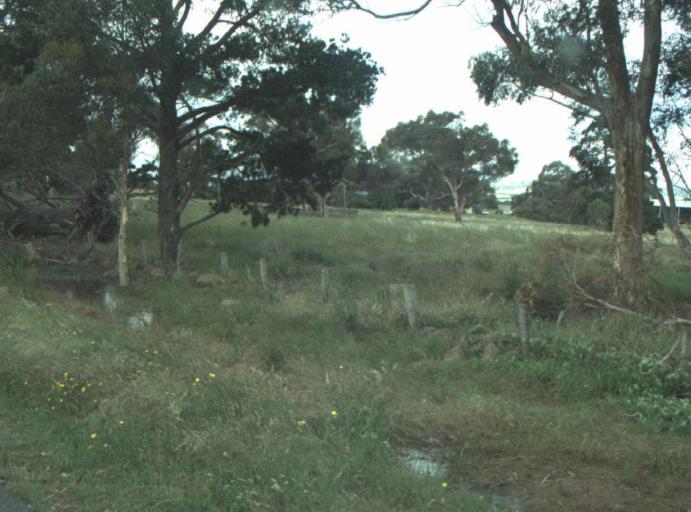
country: AU
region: Victoria
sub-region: Wyndham
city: Wyndham Vale
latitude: -37.8406
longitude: 144.3555
